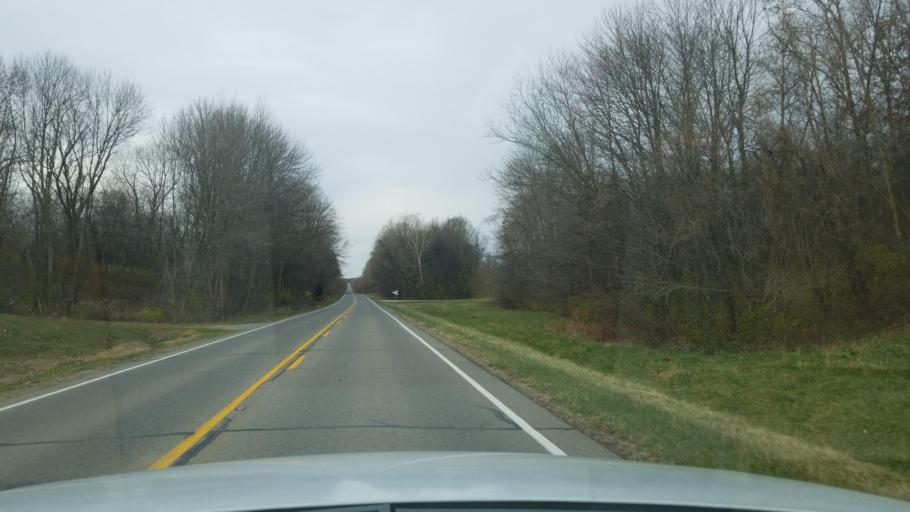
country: US
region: Indiana
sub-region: Posey County
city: Mount Vernon
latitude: 37.9290
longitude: -87.9535
